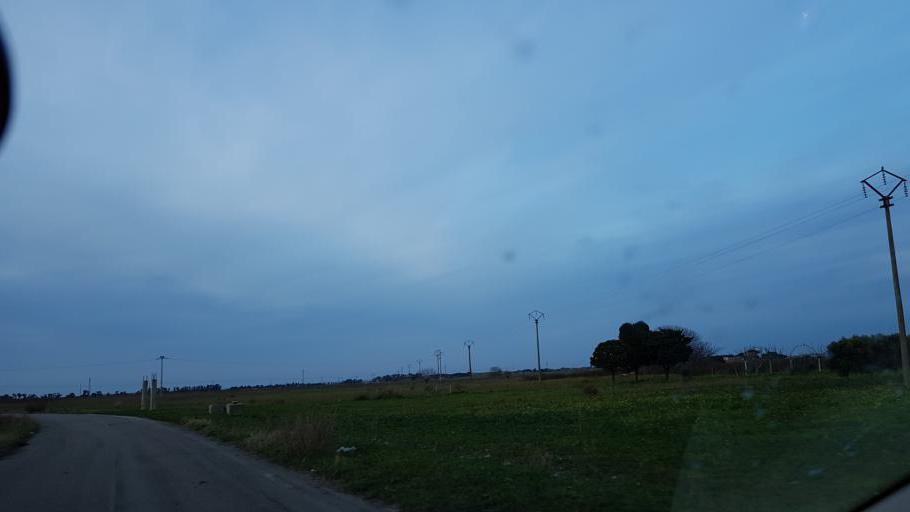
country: IT
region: Apulia
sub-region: Provincia di Brindisi
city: Brindisi
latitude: 40.6624
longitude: 17.9113
